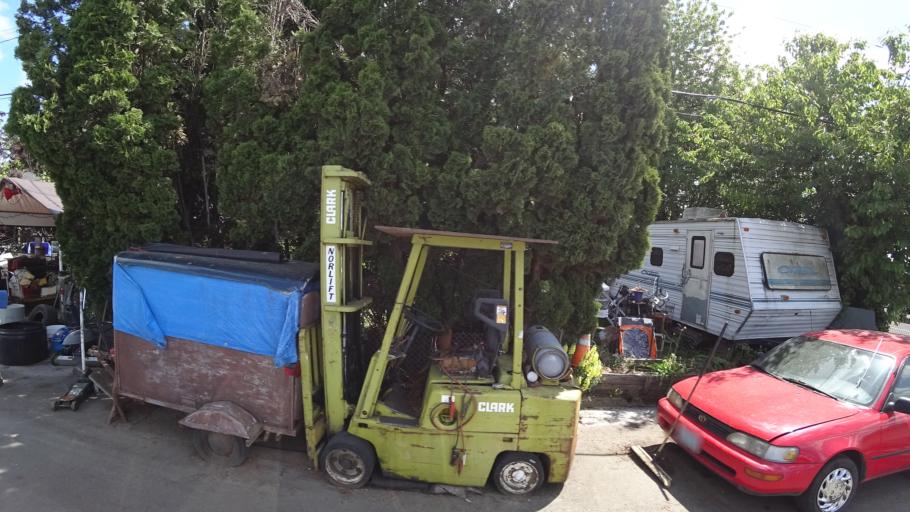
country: US
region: Oregon
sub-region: Washington County
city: Hillsboro
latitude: 45.5172
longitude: -122.9929
